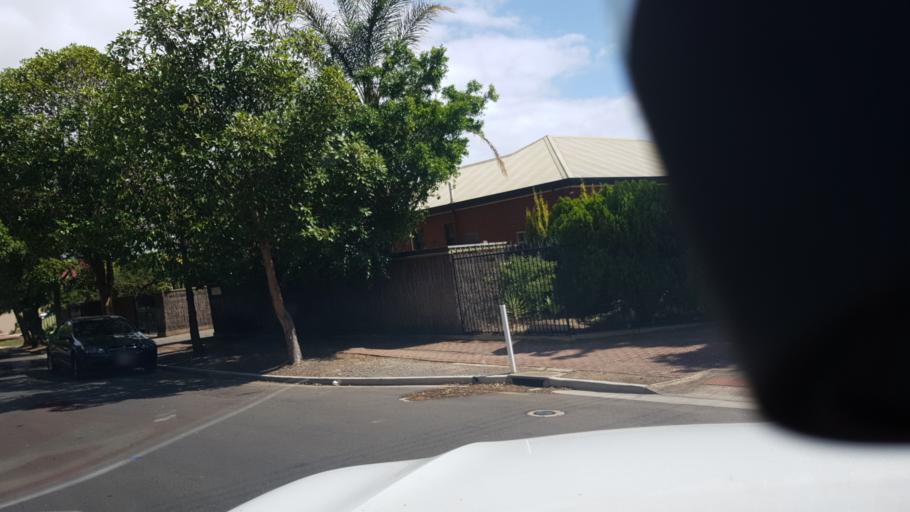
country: AU
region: South Australia
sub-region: Holdfast Bay
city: Glenelg East
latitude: -34.9758
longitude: 138.5324
